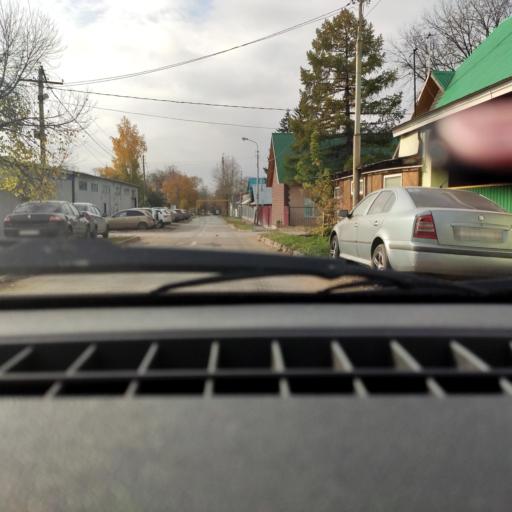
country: RU
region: Bashkortostan
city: Ufa
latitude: 54.8244
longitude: 56.0963
